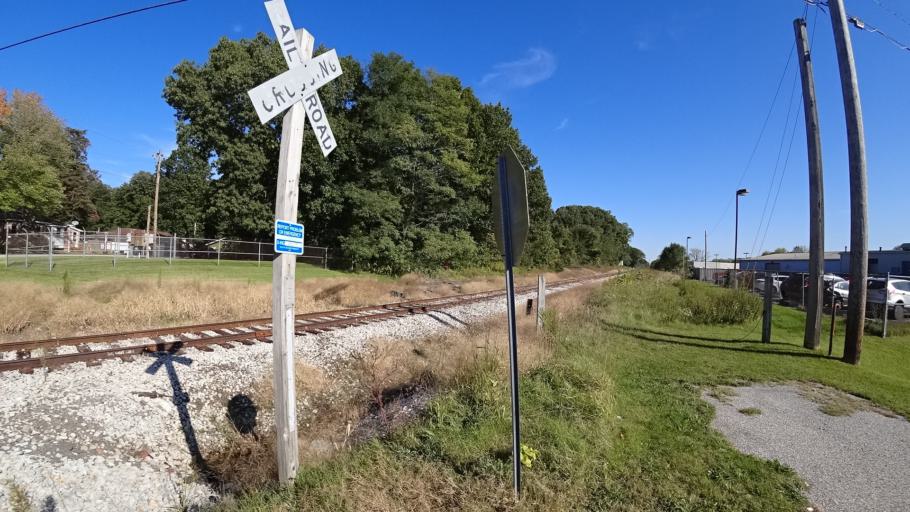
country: US
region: Indiana
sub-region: LaPorte County
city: Trail Creek
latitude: 41.7058
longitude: -86.8528
